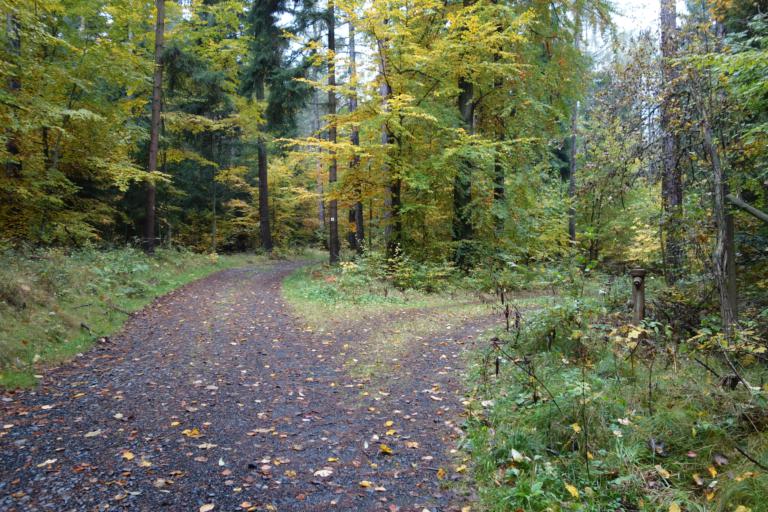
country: DE
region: Saxony
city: Kurort Oybin
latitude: 50.8367
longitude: 14.7359
